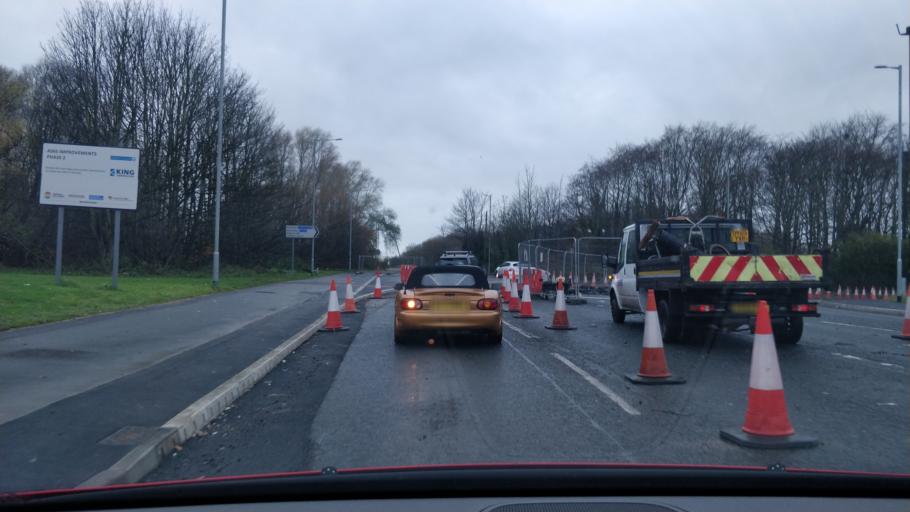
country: GB
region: England
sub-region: Sefton
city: Thornton
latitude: 53.4905
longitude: -2.9884
